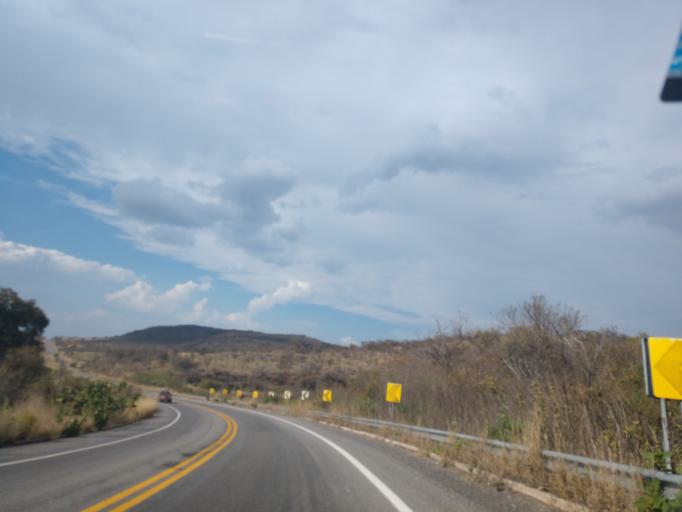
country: MX
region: Jalisco
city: La Manzanilla de la Paz
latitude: 20.0831
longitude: -103.1654
